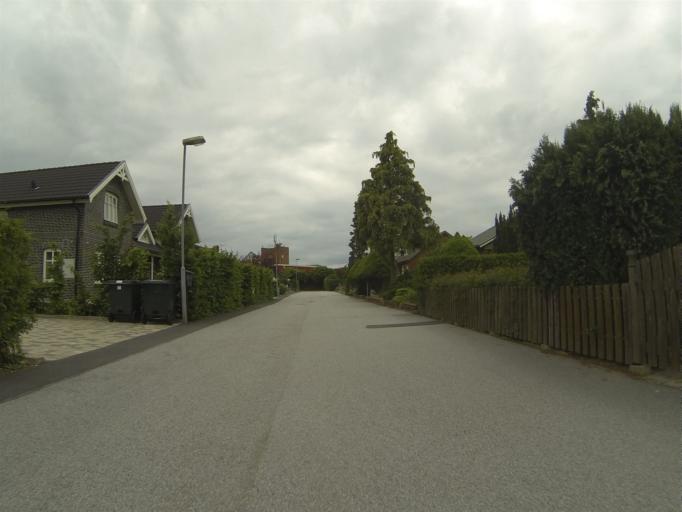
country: SE
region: Skane
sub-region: Lunds Kommun
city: Genarp
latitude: 55.7165
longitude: 13.3511
